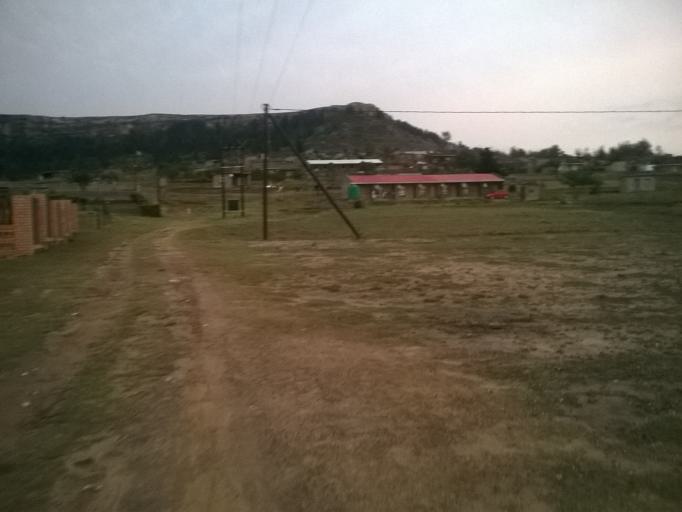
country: LS
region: Berea
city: Teyateyaneng
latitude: -29.0688
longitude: 27.7390
